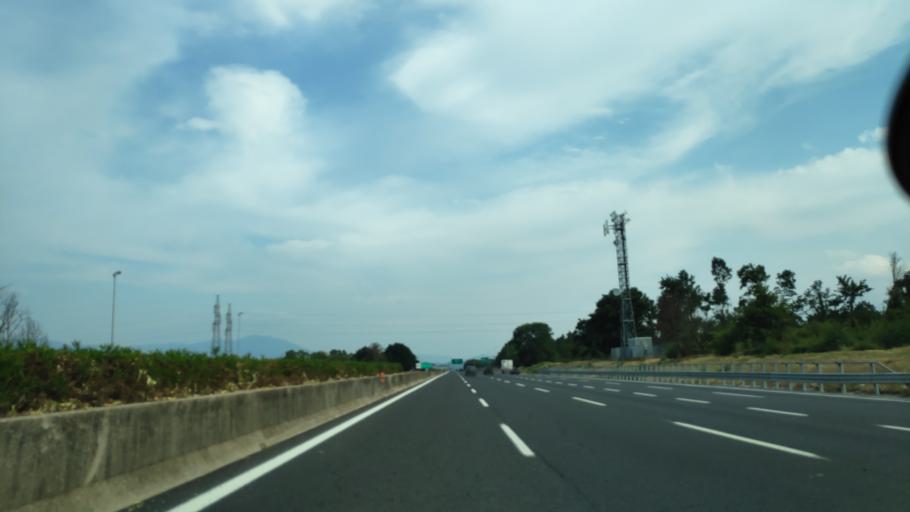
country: IT
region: Latium
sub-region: Citta metropolitana di Roma Capitale
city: Fiano Romano
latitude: 42.1708
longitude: 12.6108
